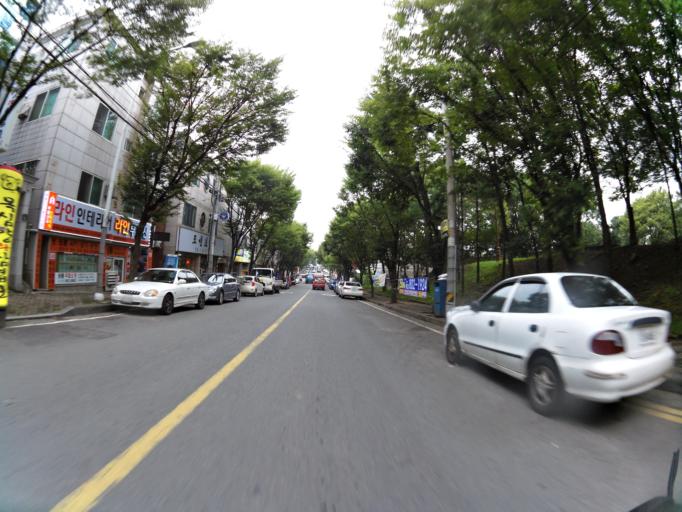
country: KR
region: Gyeongsangbuk-do
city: Gyeongsan-si
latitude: 35.8421
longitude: 128.7522
